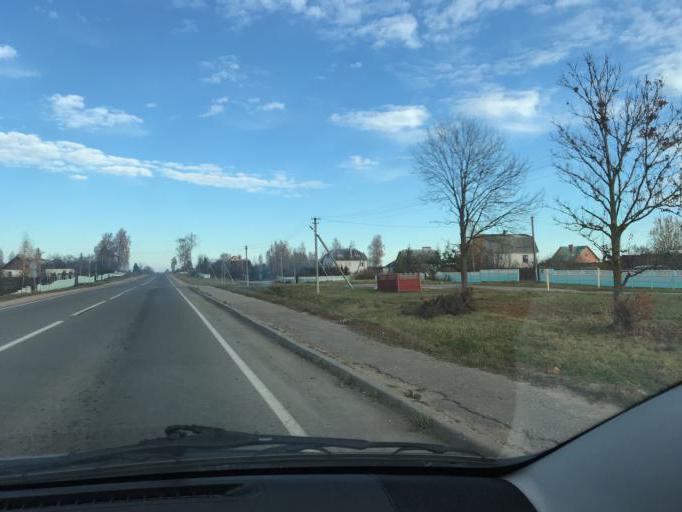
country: BY
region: Vitebsk
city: Haradok
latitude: 55.4745
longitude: 29.9694
